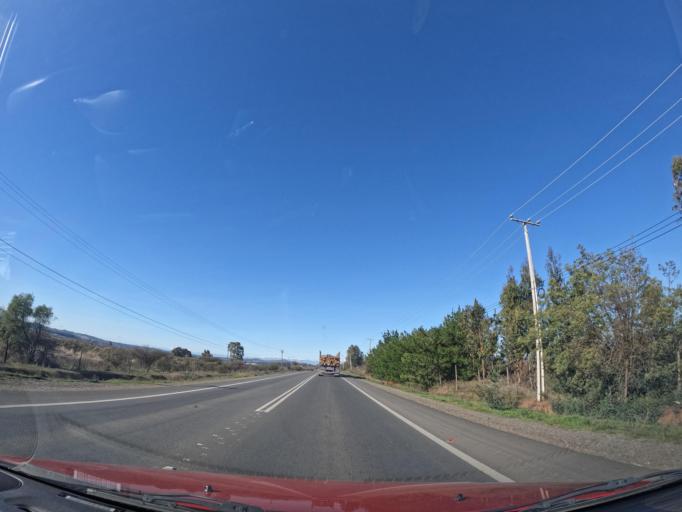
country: CL
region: Maule
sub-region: Provincia de Cauquenes
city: Cauquenes
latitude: -35.9623
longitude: -72.2470
